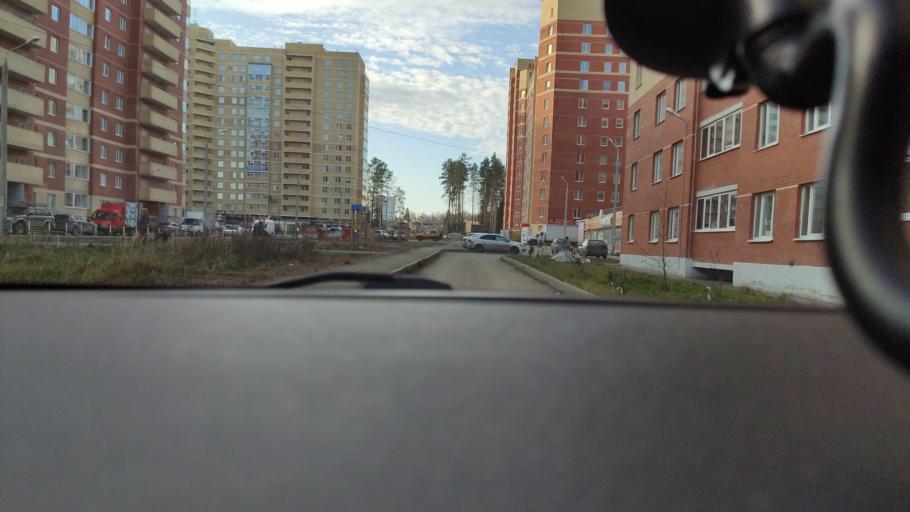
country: RU
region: Perm
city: Kondratovo
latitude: 58.0511
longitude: 56.0878
